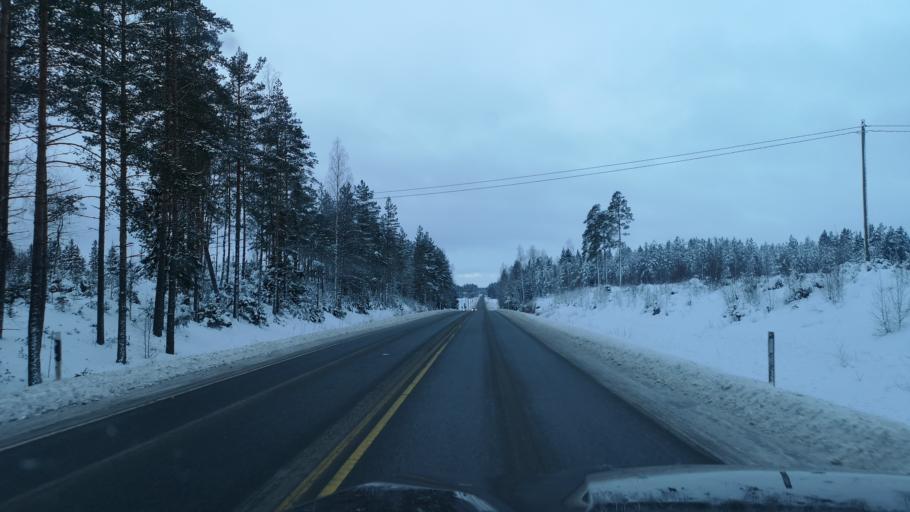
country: FI
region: Haeme
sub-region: Forssa
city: Ypaejae
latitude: 60.9205
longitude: 23.2056
